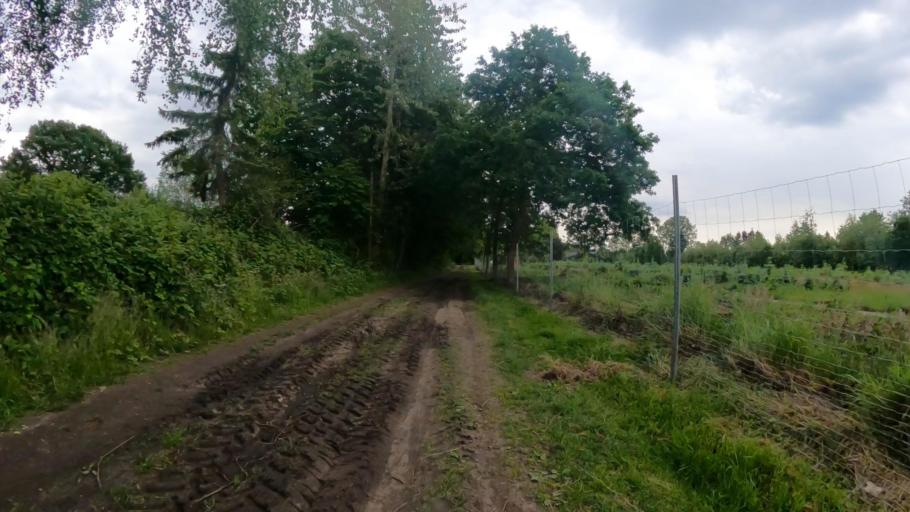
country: DE
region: Schleswig-Holstein
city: Halstenbek
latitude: 53.6357
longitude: 9.8312
